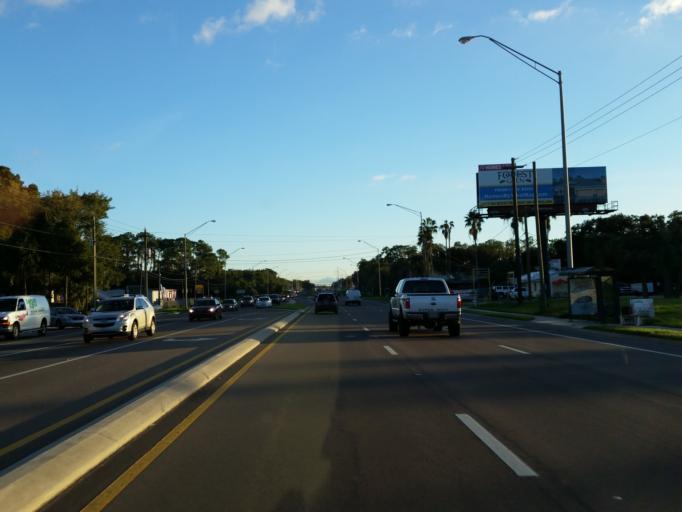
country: US
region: Florida
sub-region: Hillsborough County
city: Riverview
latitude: 27.8656
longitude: -82.3267
